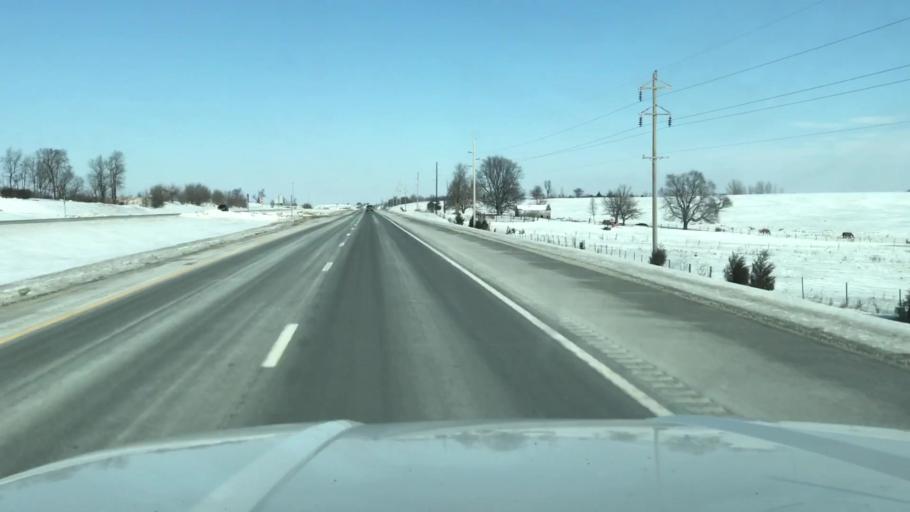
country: US
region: Missouri
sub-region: Nodaway County
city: Maryville
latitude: 40.2063
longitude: -94.8677
